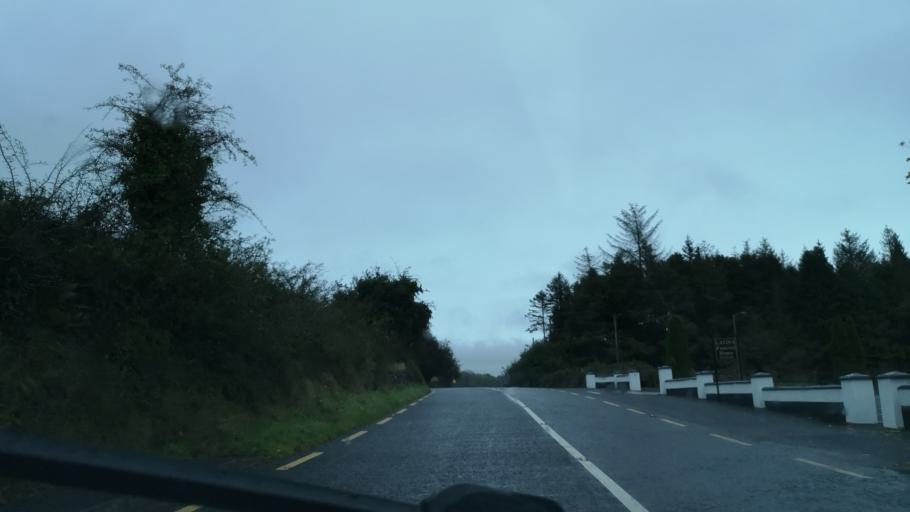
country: IE
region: Connaught
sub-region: Maigh Eo
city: Ballyhaunis
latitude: 53.7666
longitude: -8.7649
